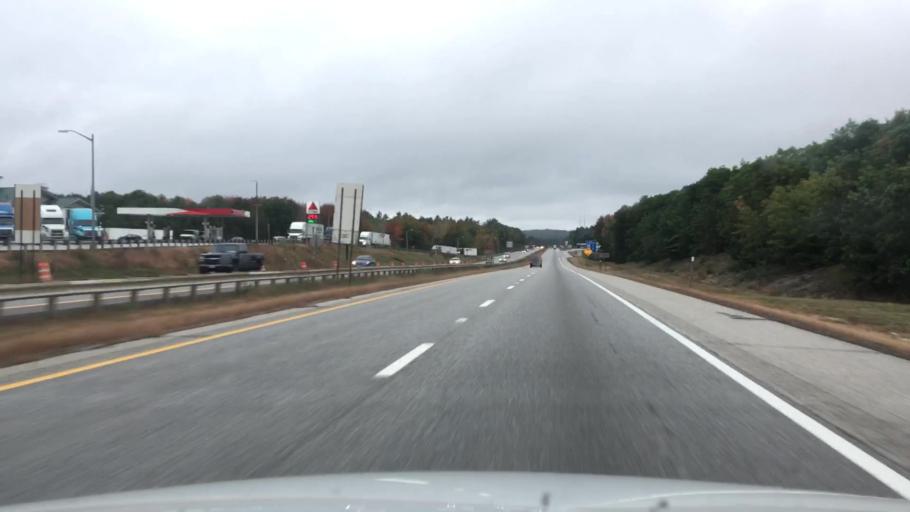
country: US
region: Maine
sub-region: Cumberland County
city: Cumberland Center
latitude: 43.8167
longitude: -70.3185
